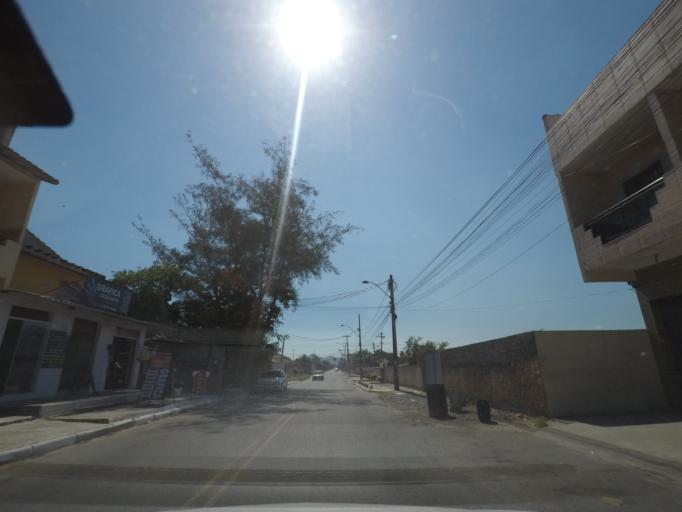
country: BR
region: Rio de Janeiro
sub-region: Marica
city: Marica
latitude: -22.9669
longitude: -42.9254
